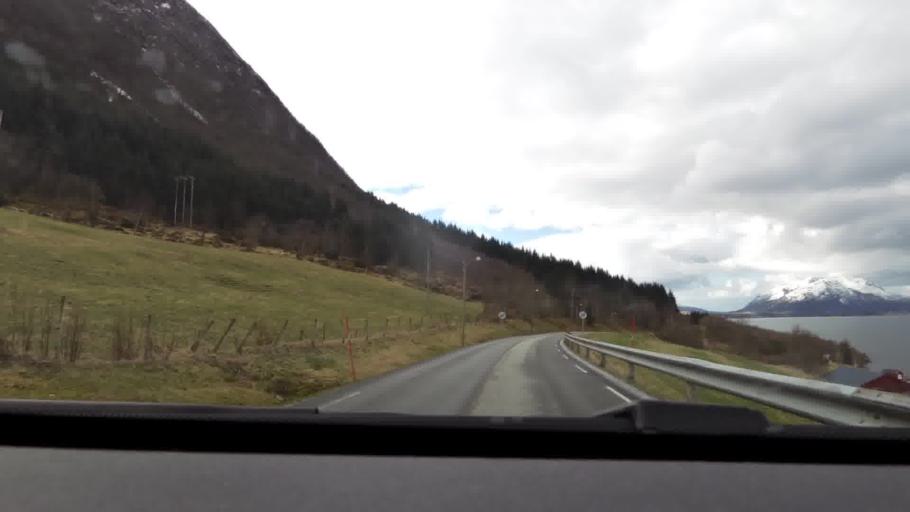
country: NO
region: More og Romsdal
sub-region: Gjemnes
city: Batnfjordsora
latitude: 62.9225
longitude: 7.5661
